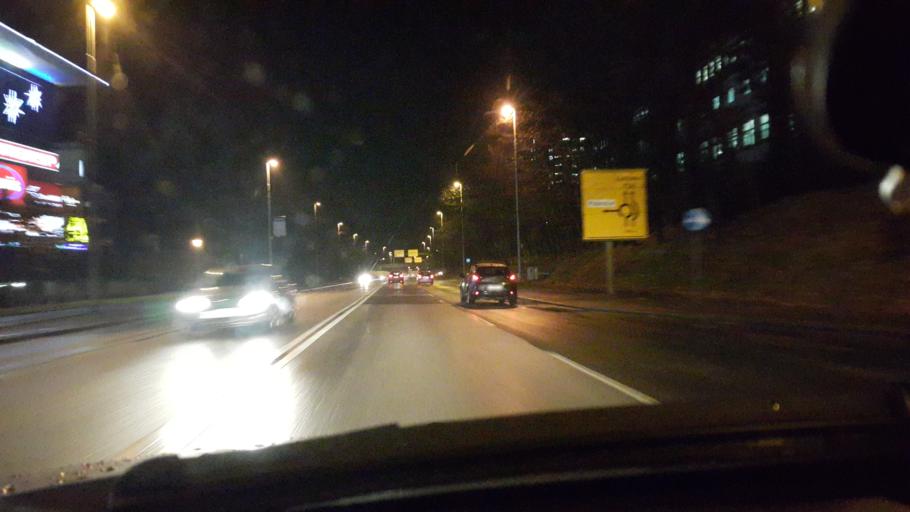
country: SI
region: Maribor
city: Maribor
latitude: 46.5543
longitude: 15.6505
